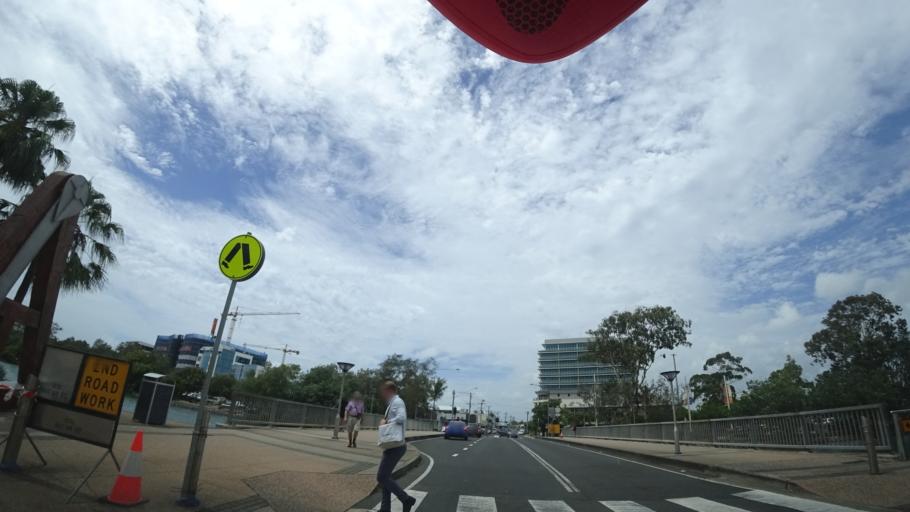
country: AU
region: Queensland
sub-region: Sunshine Coast
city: Mooloolaba
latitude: -26.6535
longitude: 153.0933
